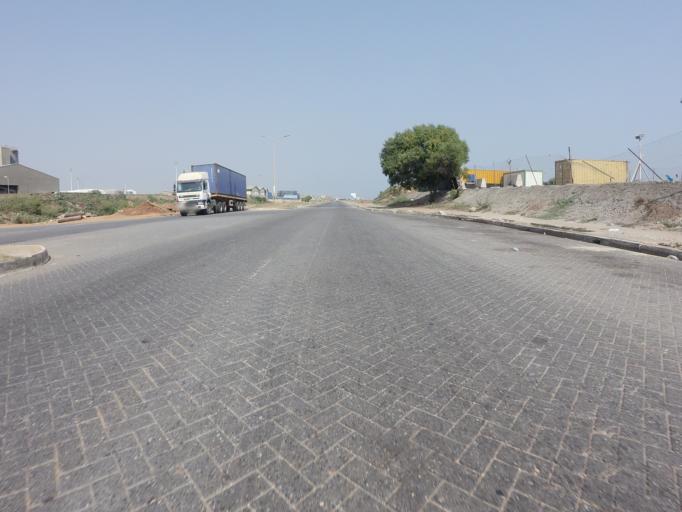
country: GH
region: Greater Accra
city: Tema
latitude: 5.6201
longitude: -0.0146
